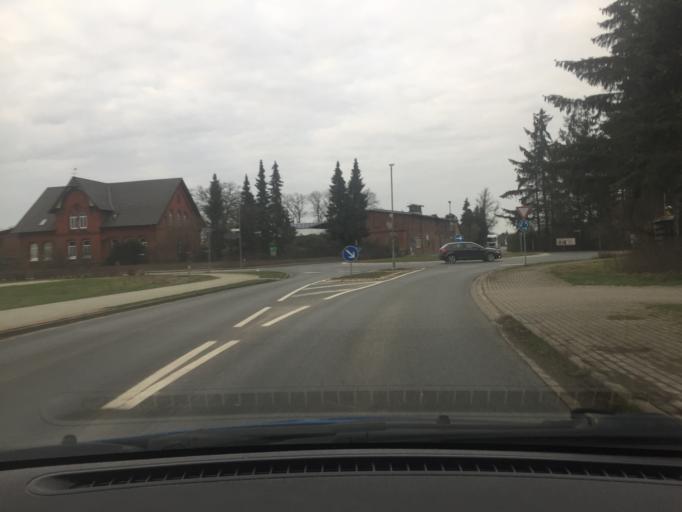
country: DE
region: Lower Saxony
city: Oetzen
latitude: 53.0055
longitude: 10.6783
